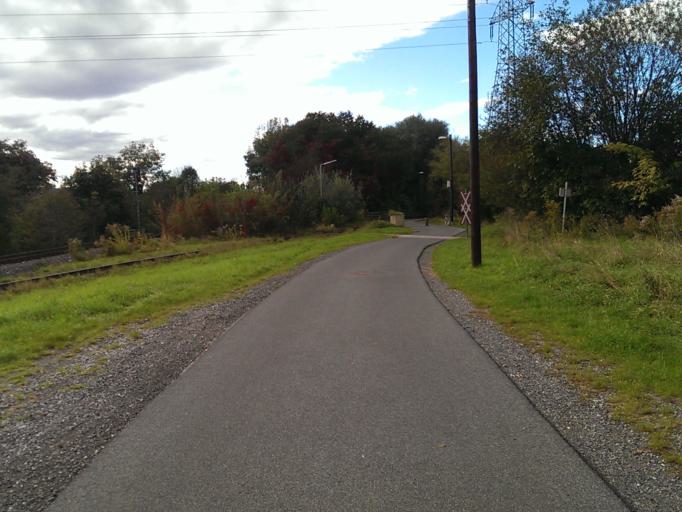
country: AT
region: Styria
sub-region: Politischer Bezirk Graz-Umgebung
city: Raaba
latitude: 47.0355
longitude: 15.4778
